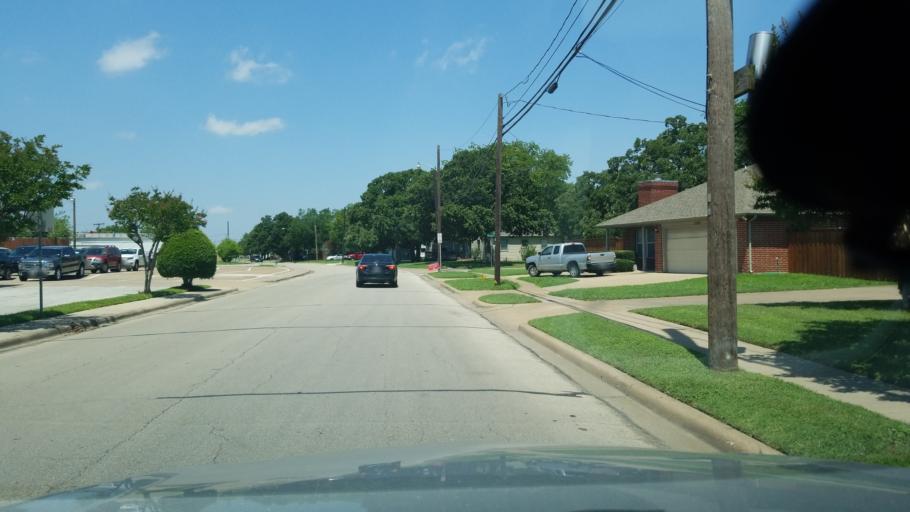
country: US
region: Texas
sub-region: Dallas County
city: Irving
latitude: 32.8222
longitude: -96.9592
